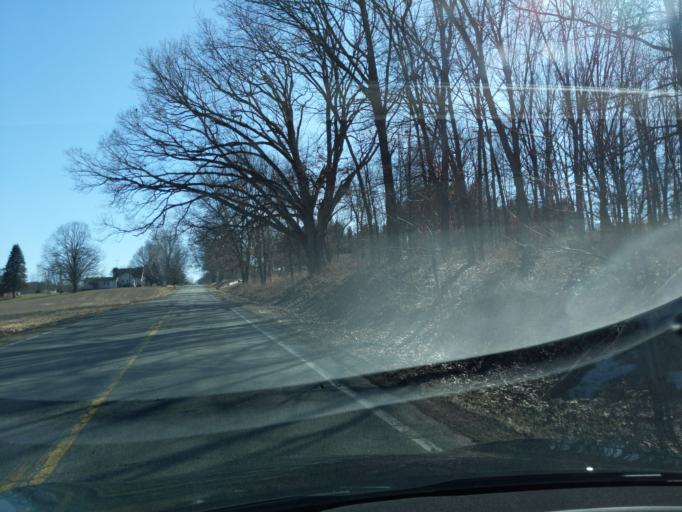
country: US
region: Michigan
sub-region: Ingham County
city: Leslie
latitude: 42.4008
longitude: -84.4433
